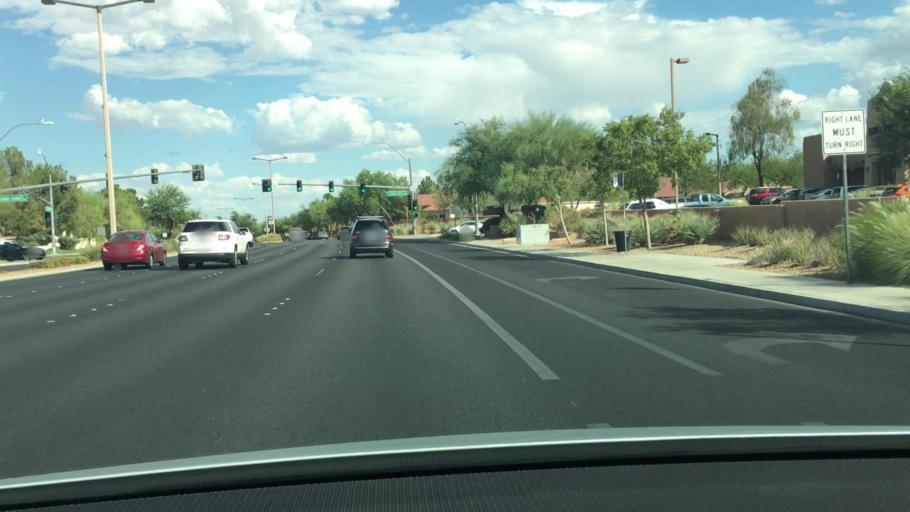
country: US
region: Nevada
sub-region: Clark County
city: Summerlin South
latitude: 36.1980
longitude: -115.2797
